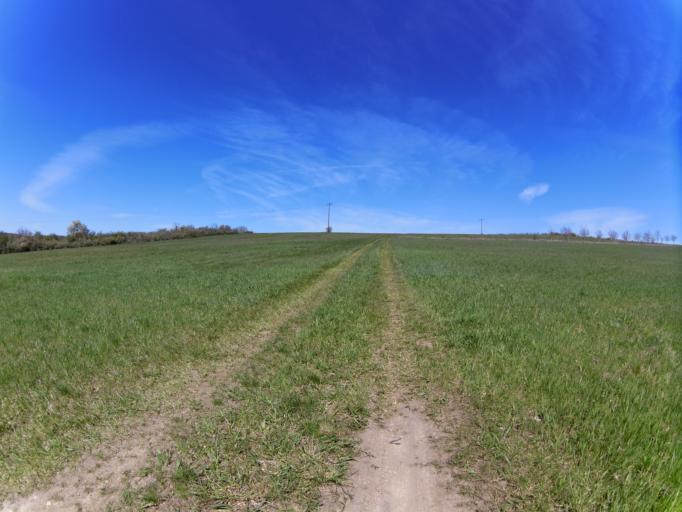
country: DE
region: Bavaria
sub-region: Regierungsbezirk Unterfranken
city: Greussenheim
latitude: 49.8115
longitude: 9.7796
